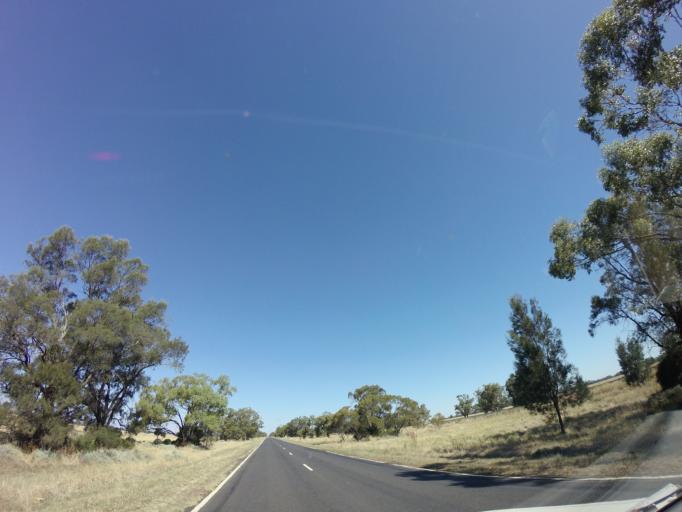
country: AU
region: New South Wales
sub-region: Bogan
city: Nyngan
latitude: -31.8051
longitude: 147.6554
